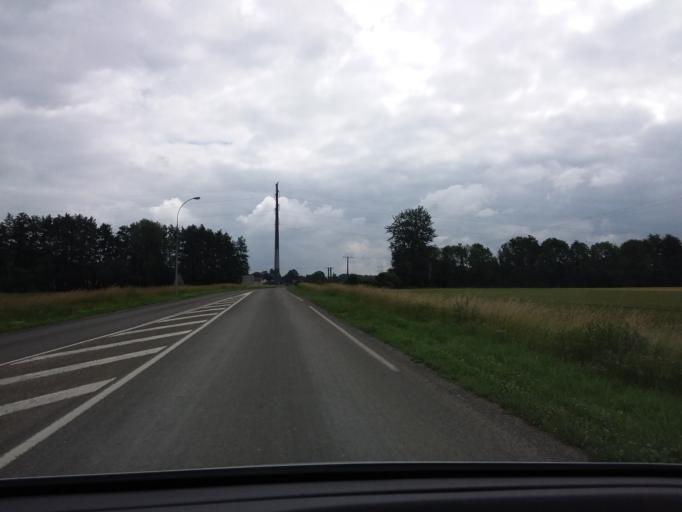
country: FR
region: Picardie
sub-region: Departement de l'Aisne
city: Bucy-le-Long
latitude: 49.3829
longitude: 3.4249
